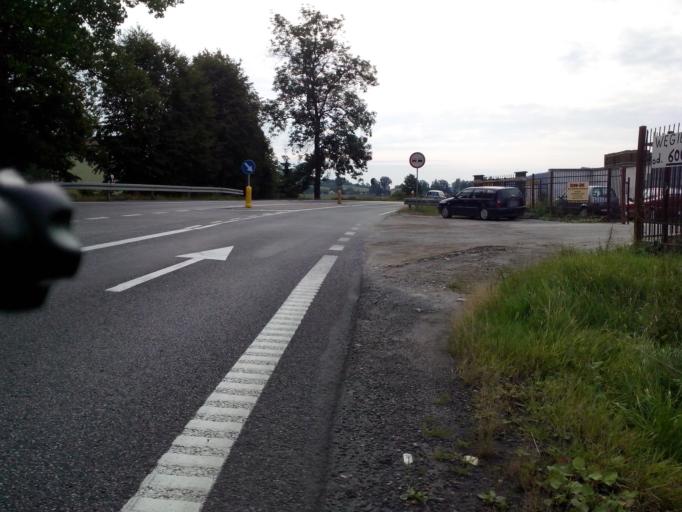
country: PL
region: Subcarpathian Voivodeship
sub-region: Powiat brzozowski
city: Domaradz
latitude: 49.8030
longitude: 21.9262
